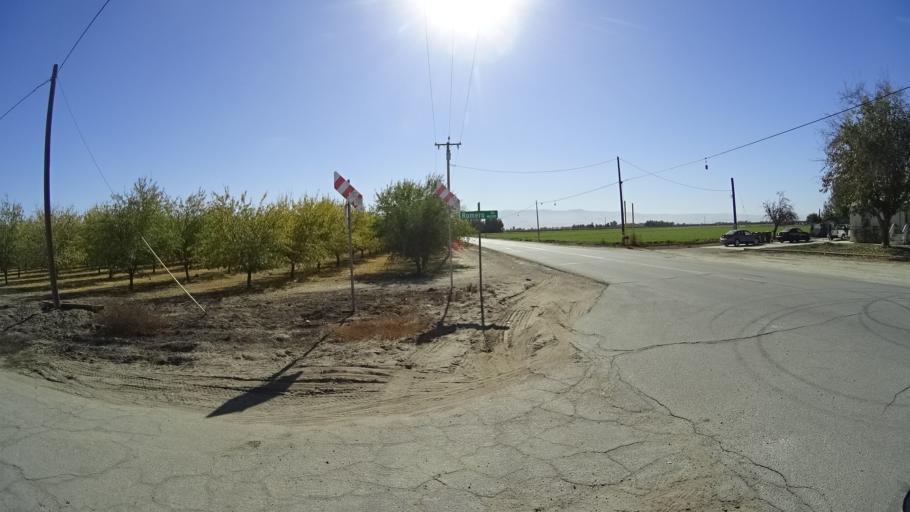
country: US
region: California
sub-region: Kern County
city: Greenfield
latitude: 35.2599
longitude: -119.0743
